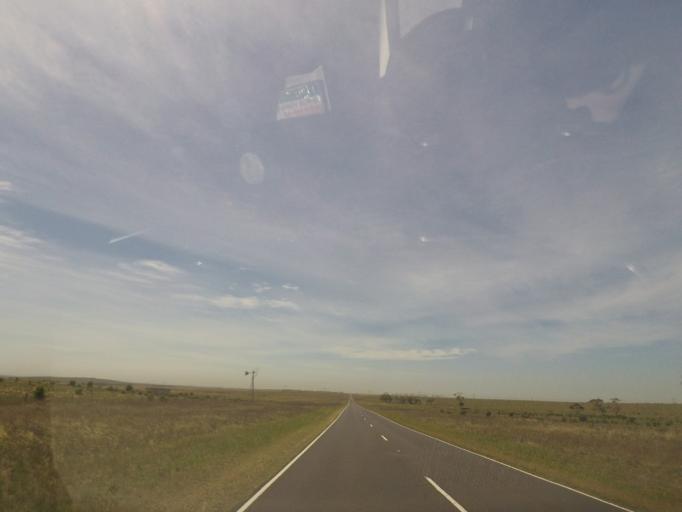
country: AU
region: Victoria
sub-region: Wyndham
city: Wyndham Vale
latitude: -37.8011
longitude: 144.4910
